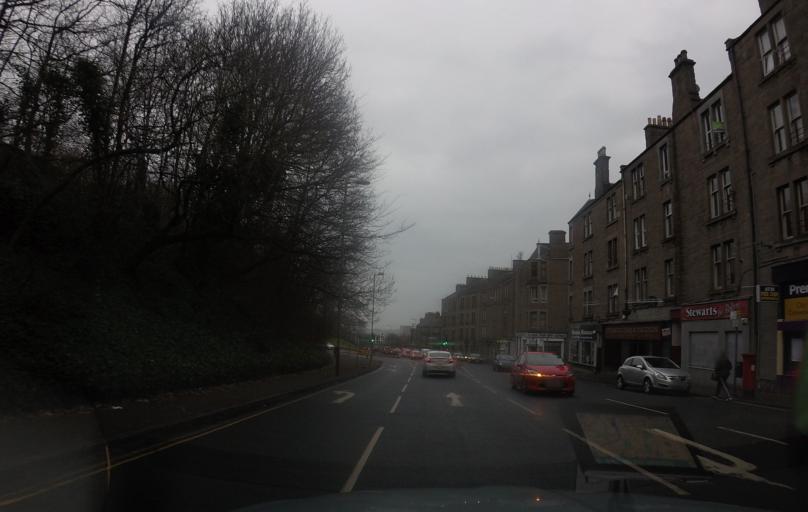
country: GB
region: Scotland
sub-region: Dundee City
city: Dundee
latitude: 56.4650
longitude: -2.9934
